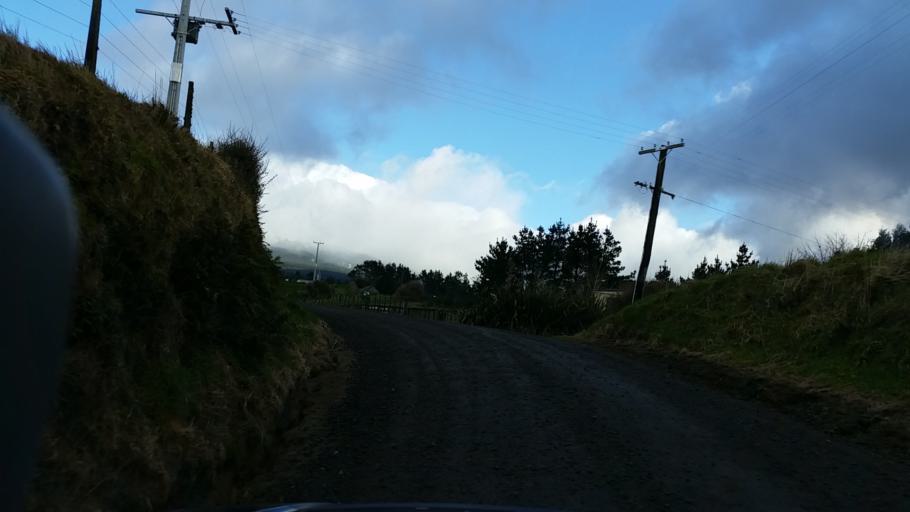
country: NZ
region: Taranaki
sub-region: South Taranaki District
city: Eltham
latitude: -39.3359
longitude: 174.1812
